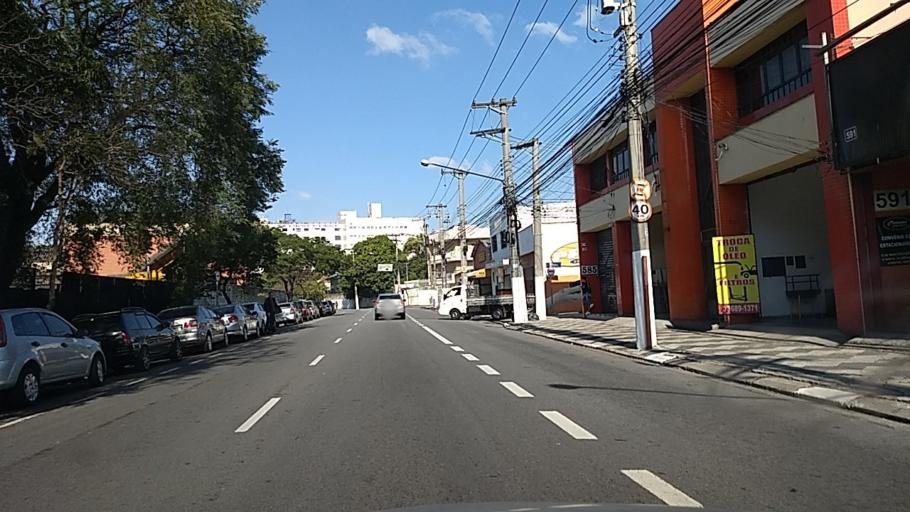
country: BR
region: Sao Paulo
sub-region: Osasco
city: Osasco
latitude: -23.5300
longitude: -46.7839
